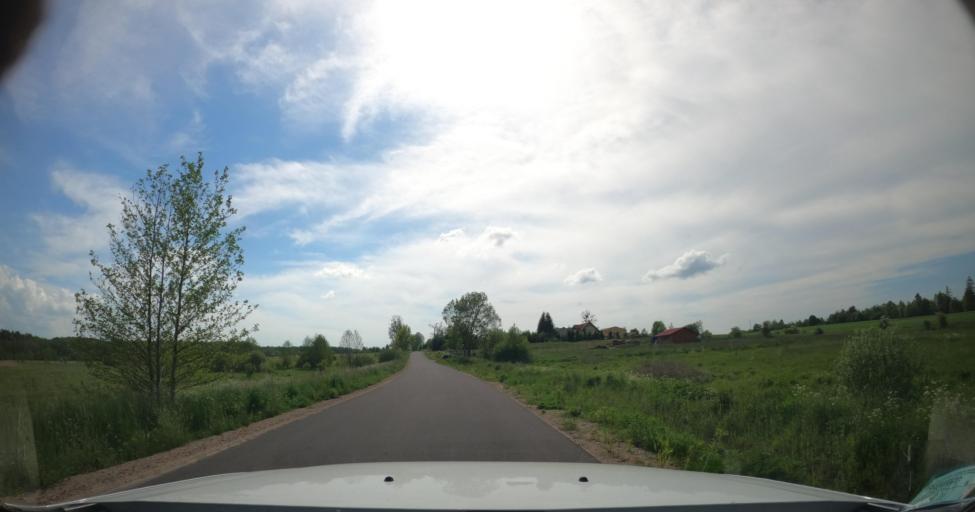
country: PL
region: Warmian-Masurian Voivodeship
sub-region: Powiat lidzbarski
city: Lidzbark Warminski
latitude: 54.1226
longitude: 20.5244
